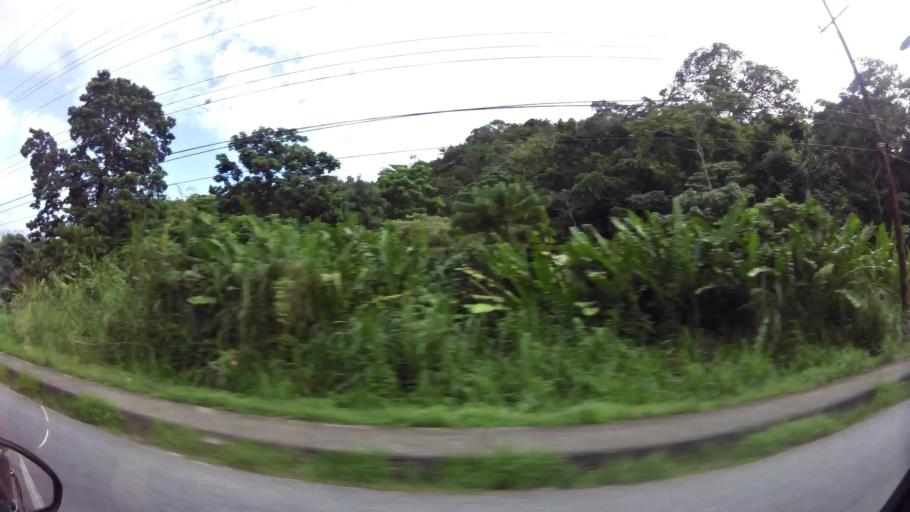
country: TT
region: Diego Martin
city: Petit Valley
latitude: 10.7148
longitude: -61.4670
